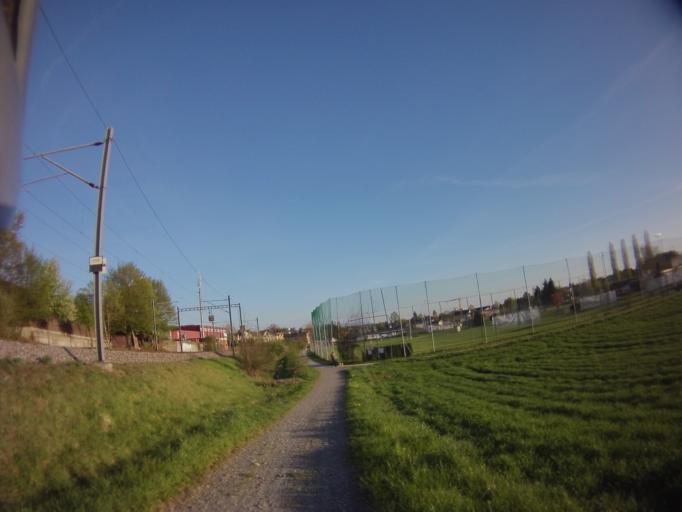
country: CH
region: Zurich
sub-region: Bezirk Affoltern
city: Affoltern / Unterdorf
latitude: 47.2876
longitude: 8.4515
